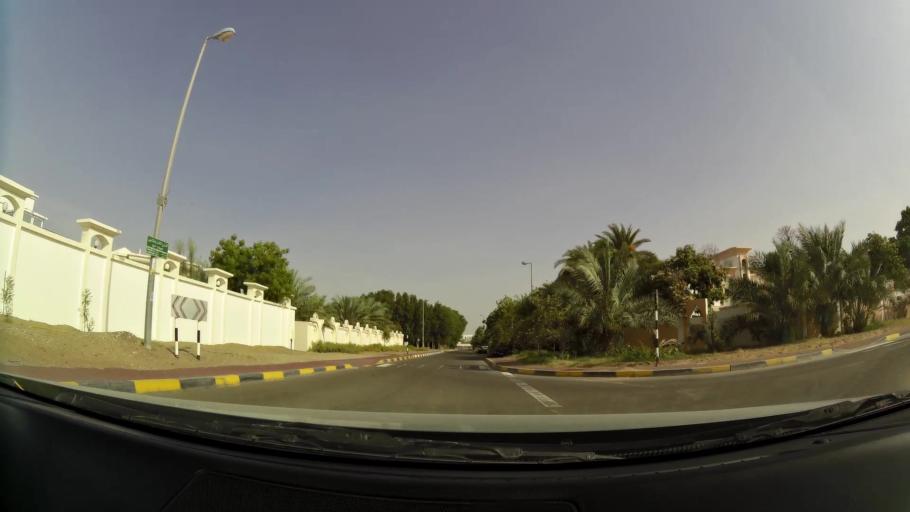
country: AE
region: Abu Dhabi
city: Al Ain
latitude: 24.2280
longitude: 55.6575
